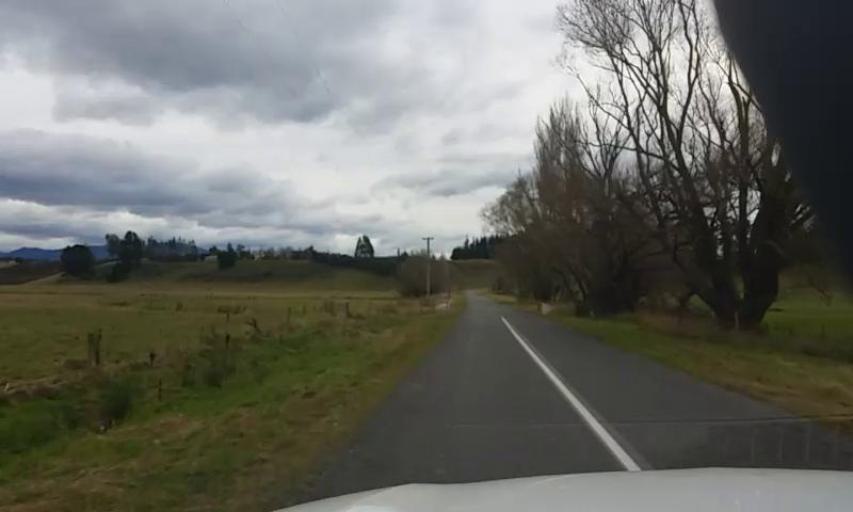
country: NZ
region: Canterbury
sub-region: Waimakariri District
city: Kaiapoi
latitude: -43.3021
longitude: 172.4379
